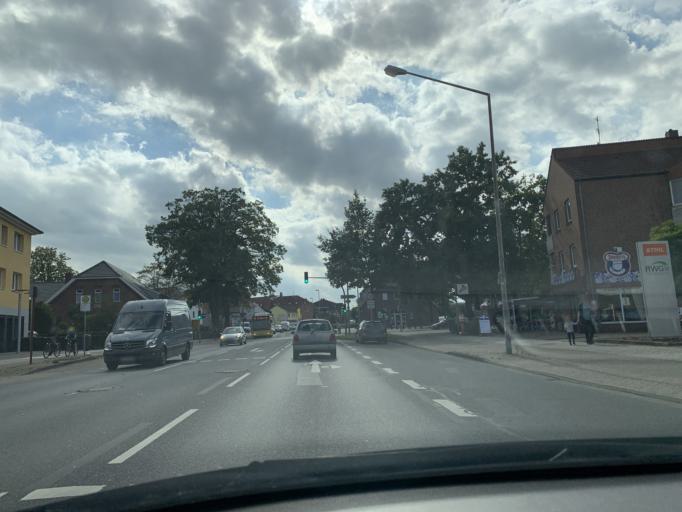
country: DE
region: Lower Saxony
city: Oldenburg
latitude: 53.1316
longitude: 8.1834
